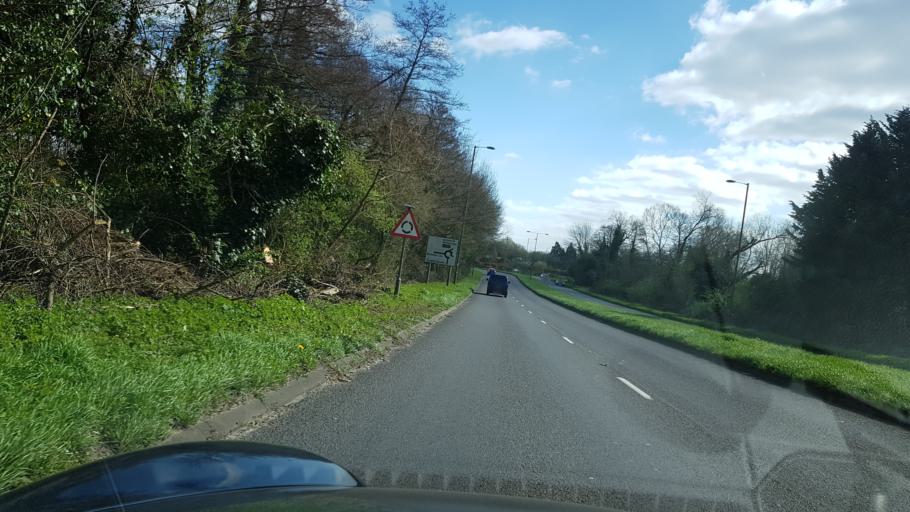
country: GB
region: England
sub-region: Surrey
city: Hale
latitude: 51.2236
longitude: -0.7809
